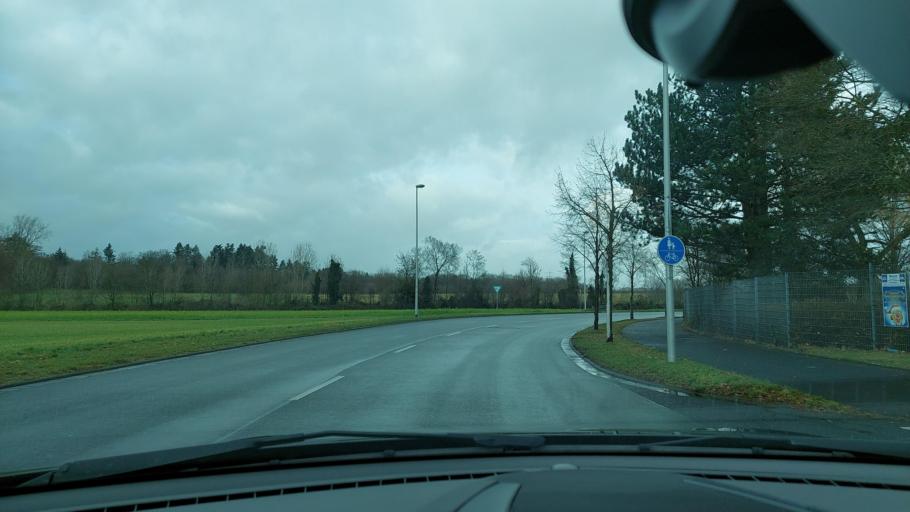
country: DE
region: North Rhine-Westphalia
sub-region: Regierungsbezirk Dusseldorf
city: Dormagen
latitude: 51.0755
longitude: 6.8074
